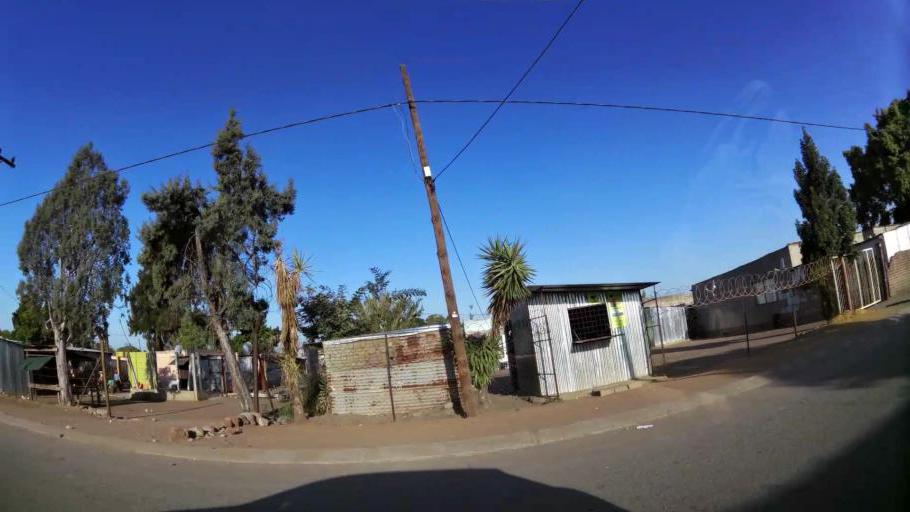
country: ZA
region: North-West
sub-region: Bojanala Platinum District Municipality
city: Rustenburg
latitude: -25.6393
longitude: 27.2201
